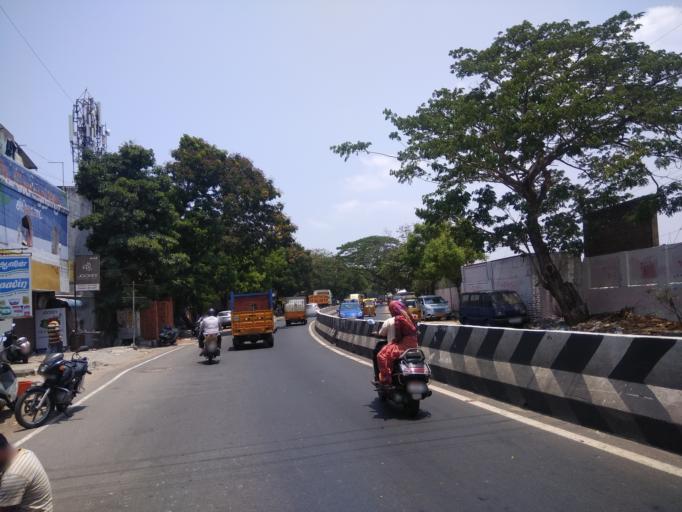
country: IN
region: Tamil Nadu
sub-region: Kancheepuram
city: Alandur
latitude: 13.0028
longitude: 80.2198
